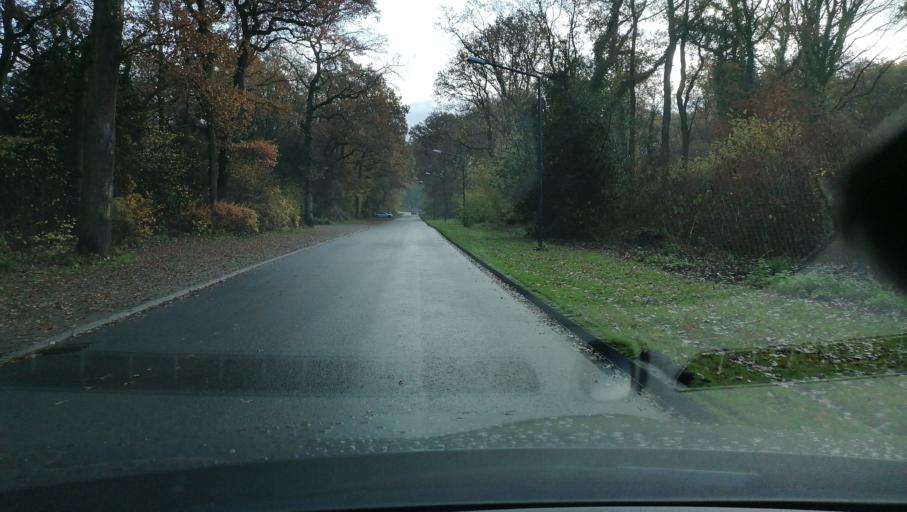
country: DE
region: North Rhine-Westphalia
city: Herten
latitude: 51.5880
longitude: 7.1583
